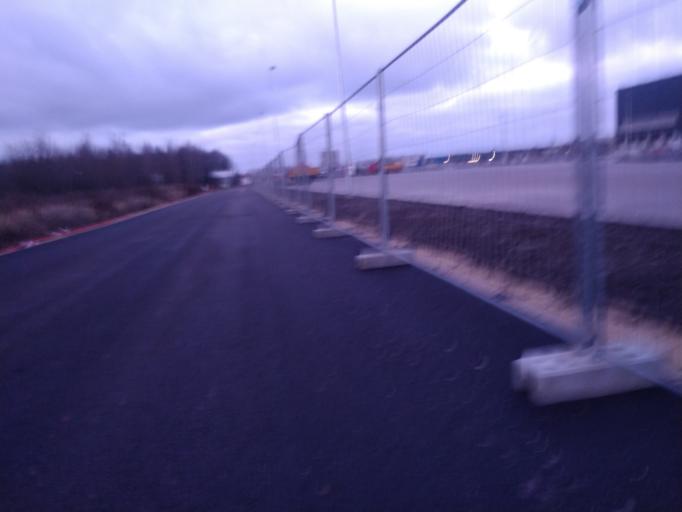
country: LV
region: Stopini
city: Ulbroka
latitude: 56.9506
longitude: 24.2314
